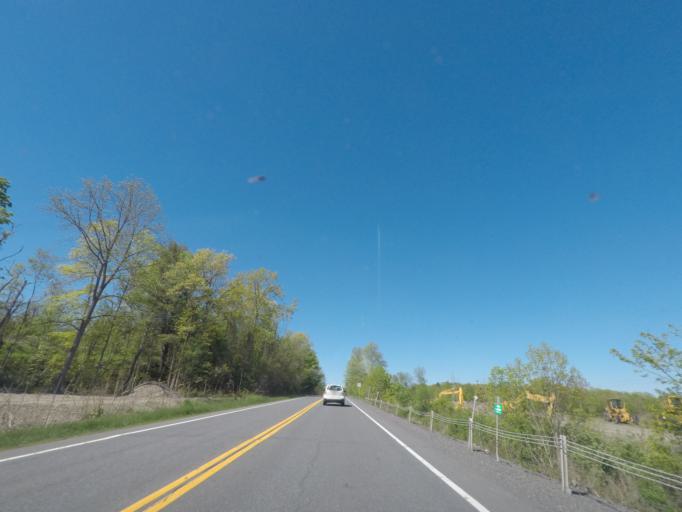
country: US
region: New York
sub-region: Greene County
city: Jefferson Heights
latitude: 42.2390
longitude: -73.8663
